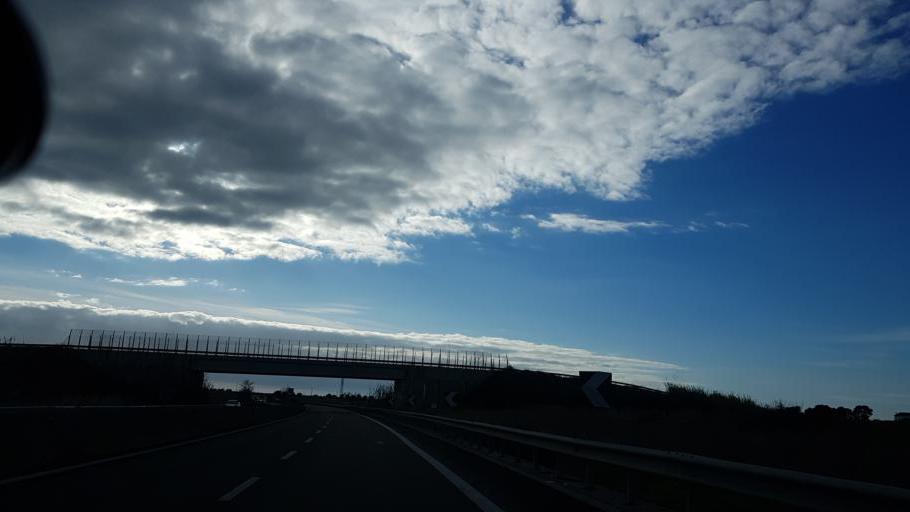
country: IT
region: Apulia
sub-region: Provincia di Brindisi
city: La Rosa
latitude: 40.6005
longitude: 17.9662
